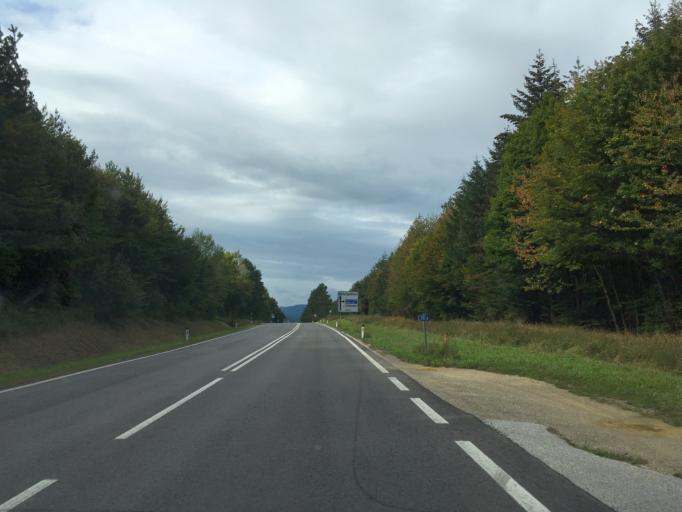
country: AT
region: Lower Austria
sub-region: Politischer Bezirk Baden
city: Heiligenkreuz
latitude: 48.0562
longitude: 16.1617
